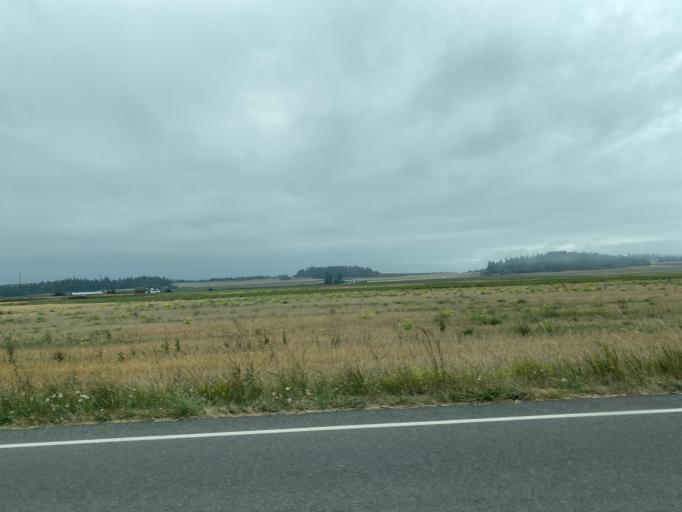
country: US
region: Washington
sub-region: Island County
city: Coupeville
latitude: 48.2015
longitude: -122.6966
